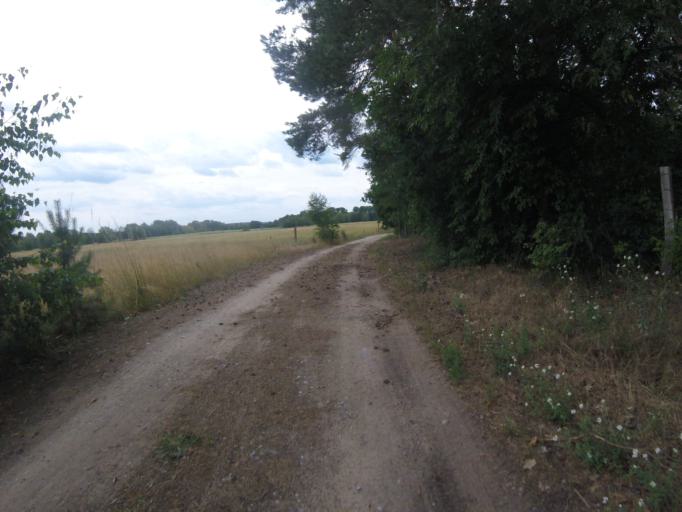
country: DE
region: Brandenburg
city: Bestensee
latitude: 52.2565
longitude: 13.6997
